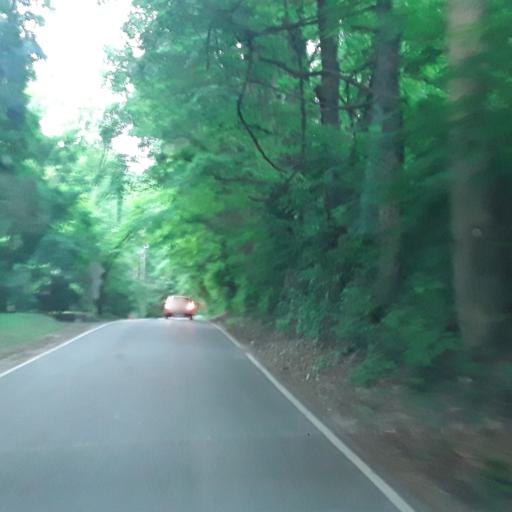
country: US
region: Tennessee
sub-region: Williamson County
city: Brentwood
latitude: 36.0508
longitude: -86.7637
